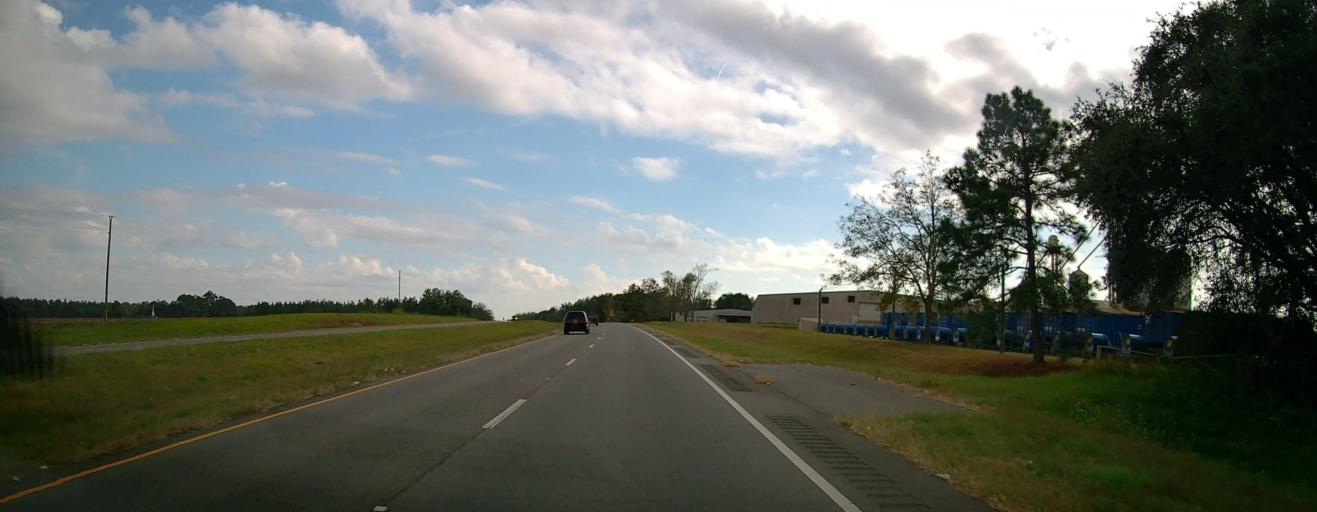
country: US
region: Georgia
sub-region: Thomas County
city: Meigs
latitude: 31.0479
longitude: -84.0706
